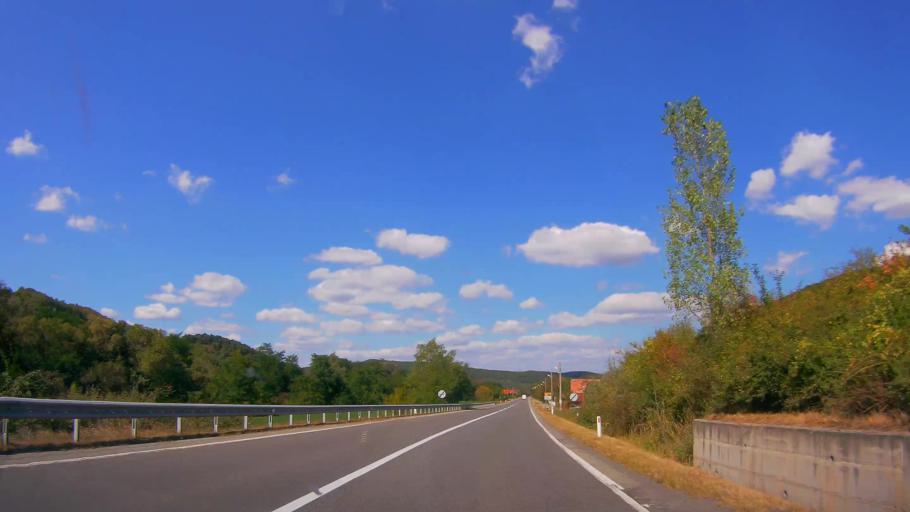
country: RO
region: Salaj
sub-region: Comuna Zimbor
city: Zimbor
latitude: 46.9781
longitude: 23.2531
